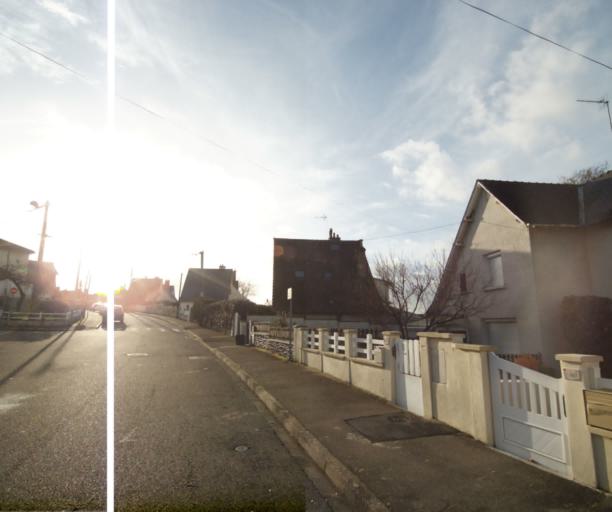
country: FR
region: Pays de la Loire
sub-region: Departement de la Sarthe
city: Le Mans
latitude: 47.9624
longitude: 0.2019
